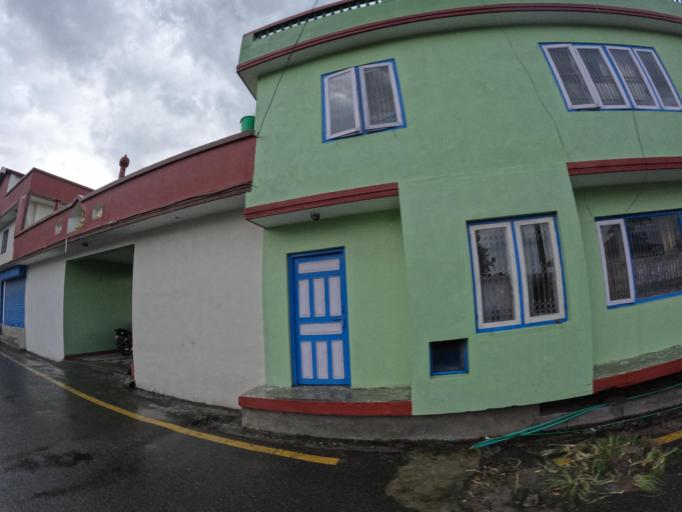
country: NP
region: Central Region
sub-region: Bagmati Zone
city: Kathmandu
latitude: 27.7739
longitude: 85.3371
